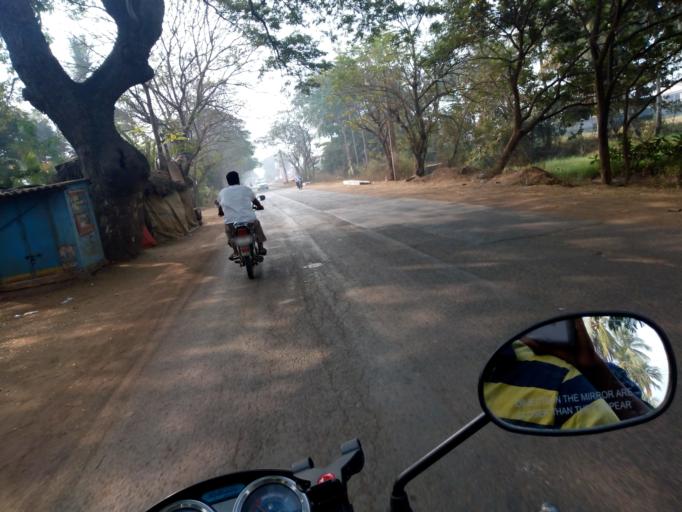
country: IN
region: Andhra Pradesh
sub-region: West Godavari
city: Tadepallegudem
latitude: 16.8123
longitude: 81.4082
